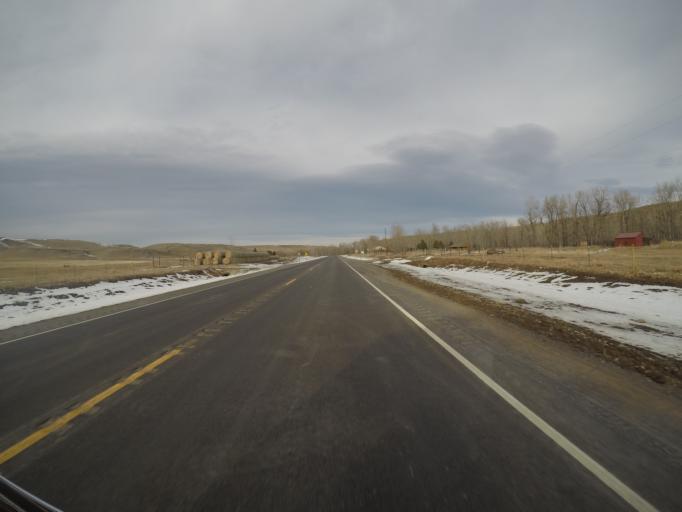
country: US
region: Montana
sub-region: Stillwater County
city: Absarokee
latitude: 45.4255
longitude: -109.4709
